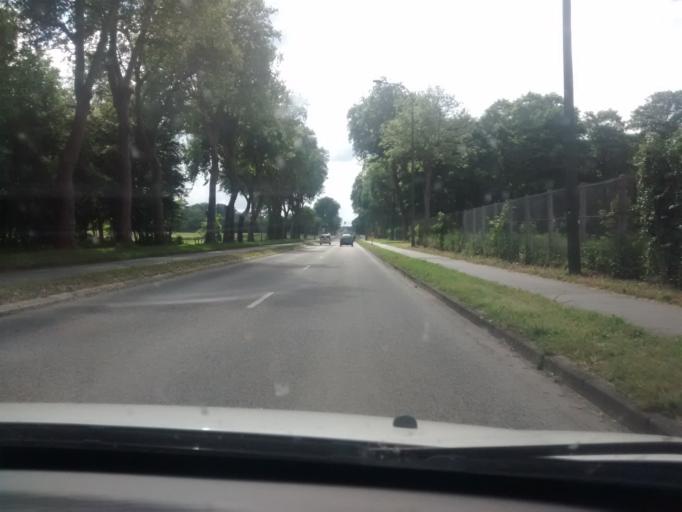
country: FR
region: Ile-de-France
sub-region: Departement des Yvelines
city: Saint-Cyr-l'Ecole
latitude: 48.8016
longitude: 2.0843
